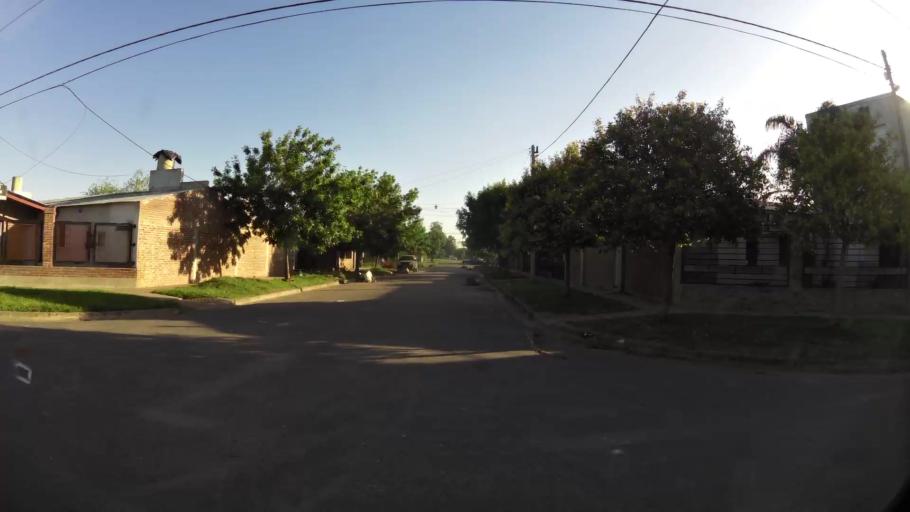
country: AR
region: Santa Fe
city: Santa Fe de la Vera Cruz
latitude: -31.5923
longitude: -60.6823
